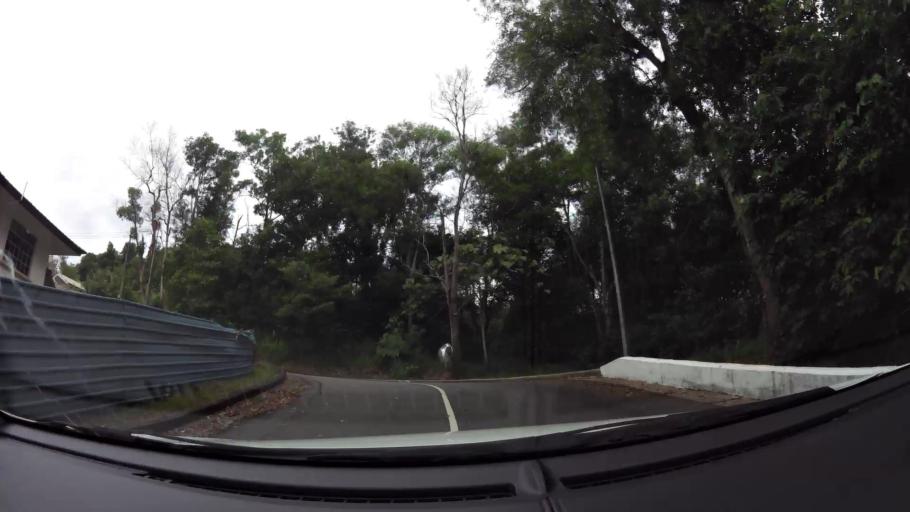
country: BN
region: Brunei and Muara
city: Bandar Seri Begawan
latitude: 4.8864
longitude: 114.9070
